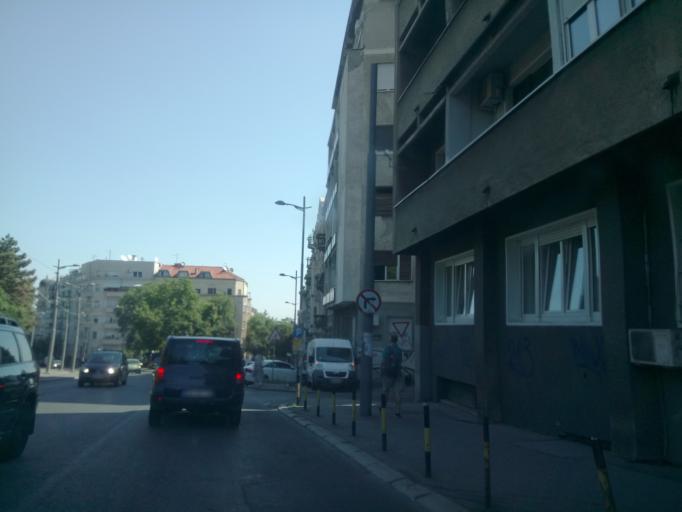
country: RS
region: Central Serbia
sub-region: Belgrade
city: Stari Grad
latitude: 44.8219
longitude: 20.4550
